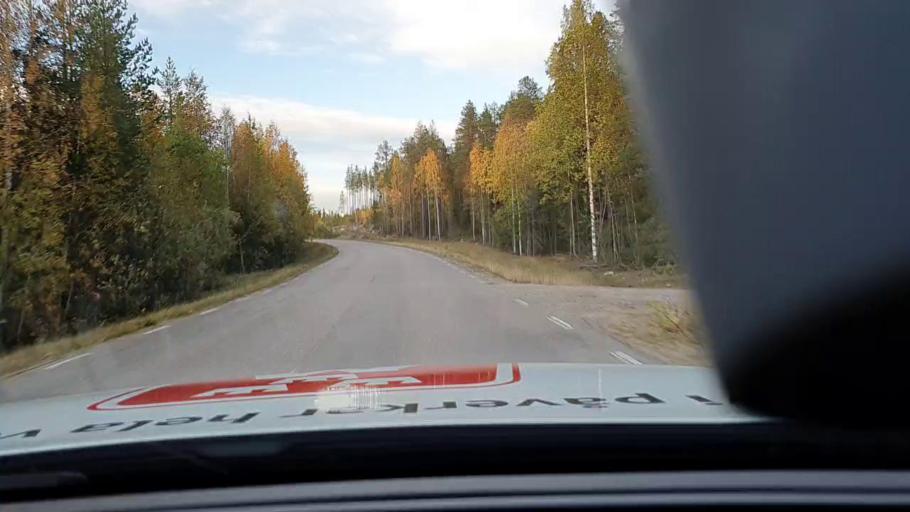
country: SE
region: Norrbotten
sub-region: Overkalix Kommun
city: OEverkalix
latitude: 66.3247
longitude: 22.7666
